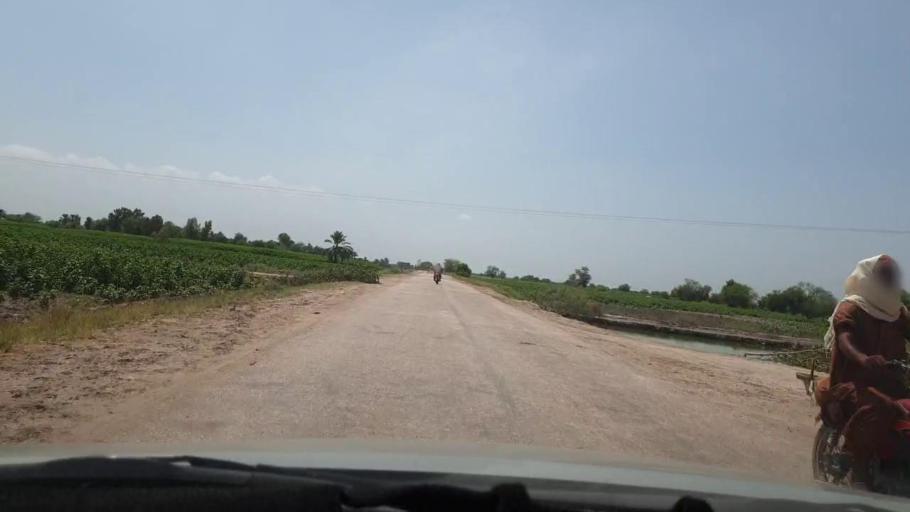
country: PK
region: Sindh
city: Pano Aqil
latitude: 27.6635
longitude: 69.1325
